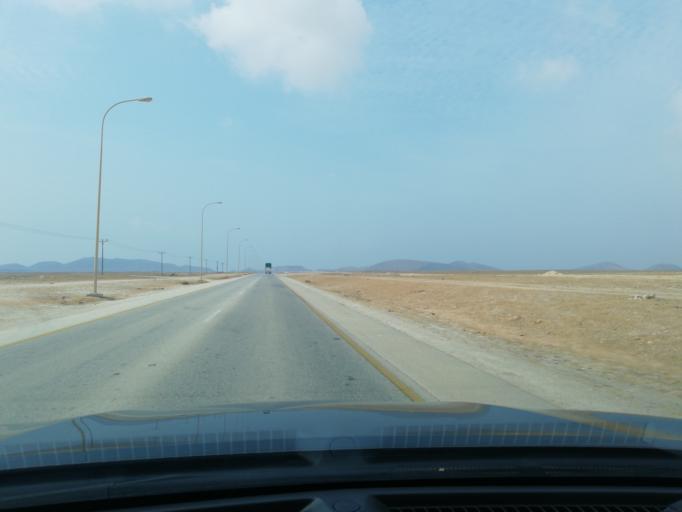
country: OM
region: Zufar
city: Salalah
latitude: 16.9328
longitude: 53.8433
